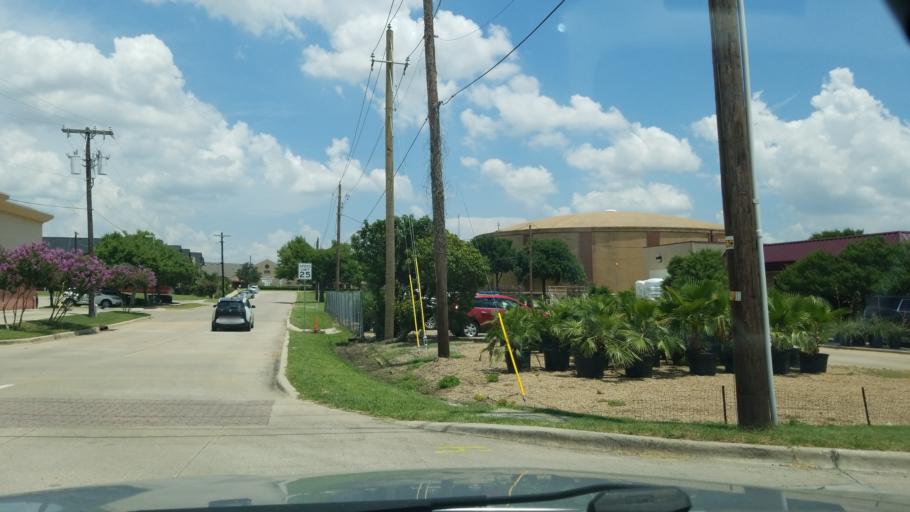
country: US
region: Texas
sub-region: Dallas County
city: Coppell
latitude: 32.9694
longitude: -96.9586
